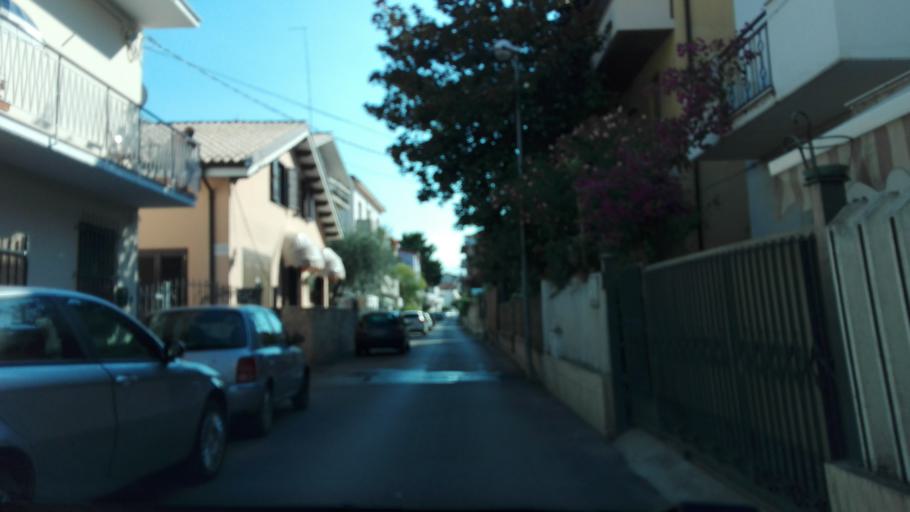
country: IT
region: Abruzzo
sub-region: Provincia di Pescara
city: Montesilvano Marina
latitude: 42.5122
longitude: 14.1544
